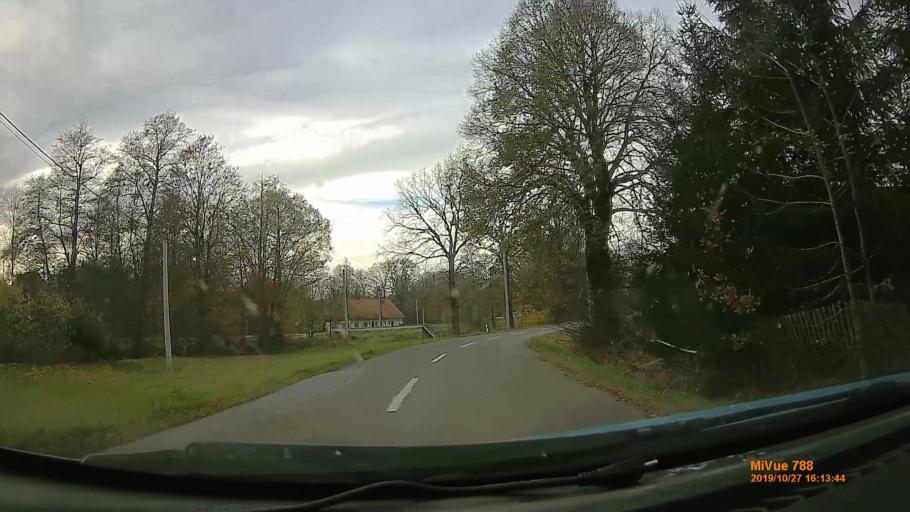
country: PL
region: Lower Silesian Voivodeship
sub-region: Powiat klodzki
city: Radkow
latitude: 50.5512
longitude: 16.4011
